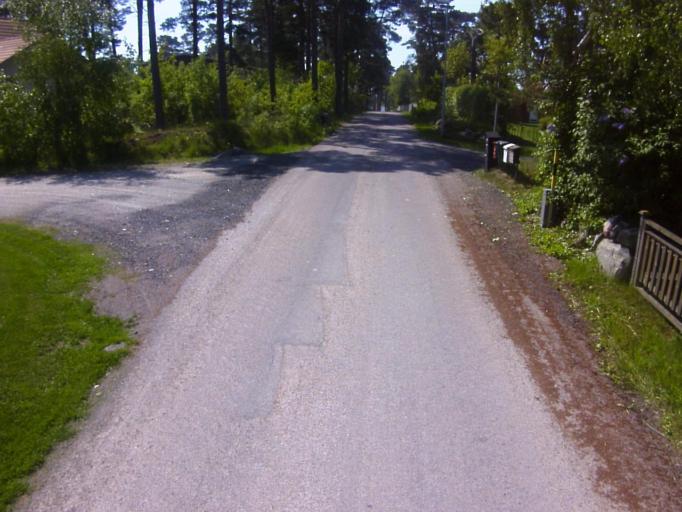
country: SE
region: Blekinge
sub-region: Solvesborgs Kommun
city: Soelvesborg
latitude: 56.0164
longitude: 14.7093
